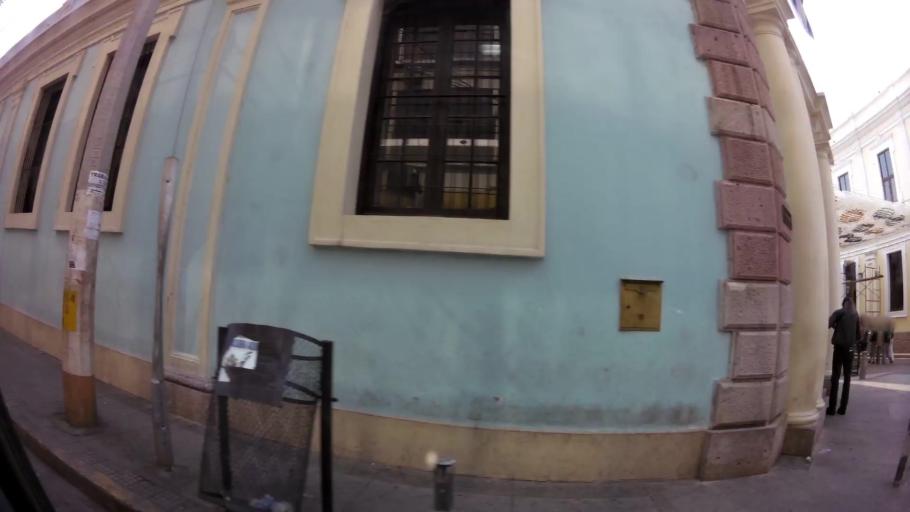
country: HN
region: Francisco Morazan
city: Tegucigalpa
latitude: 14.1064
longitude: -87.2078
